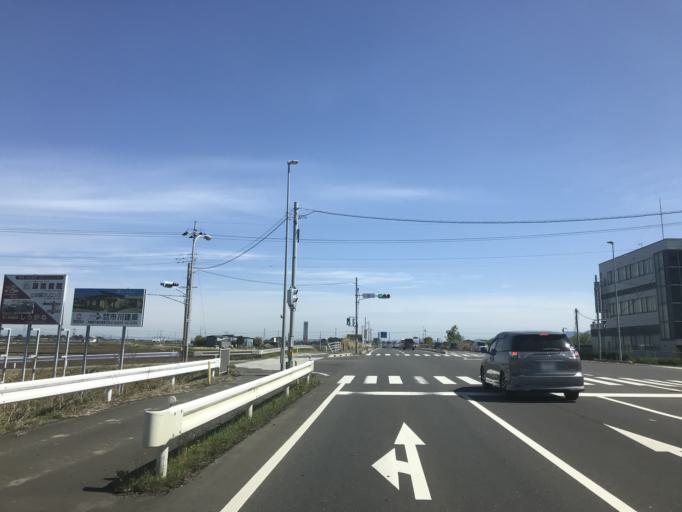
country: JP
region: Ibaraki
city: Ishige
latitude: 36.1476
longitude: 139.9907
